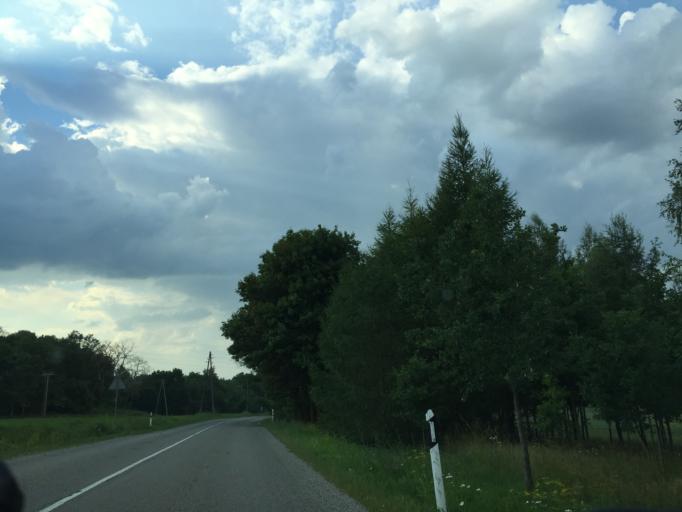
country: LV
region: Dobeles Rajons
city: Dobele
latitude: 56.5983
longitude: 23.3087
